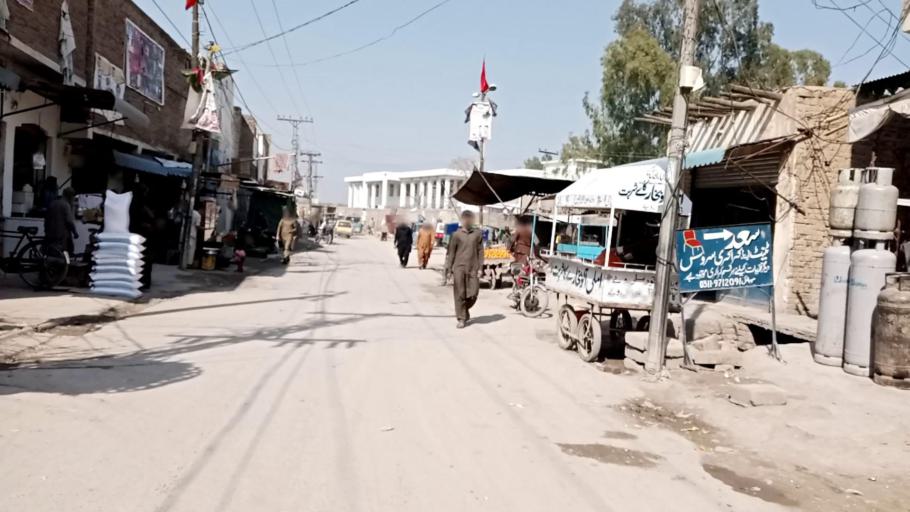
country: PK
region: Khyber Pakhtunkhwa
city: Peshawar
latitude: 34.0129
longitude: 71.5138
